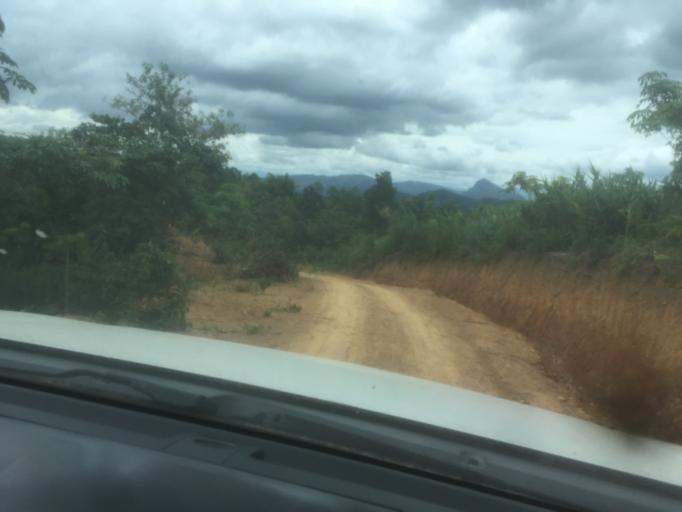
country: LA
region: Phongsali
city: Khoa
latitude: 20.9271
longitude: 102.5484
